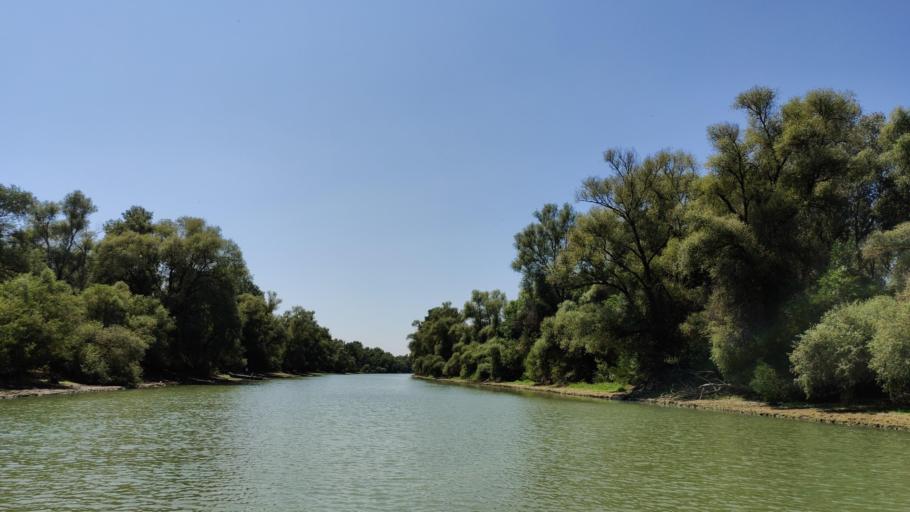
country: RO
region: Tulcea
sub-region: Comuna Nufaru
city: Nufaru
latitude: 45.2268
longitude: 28.8882
